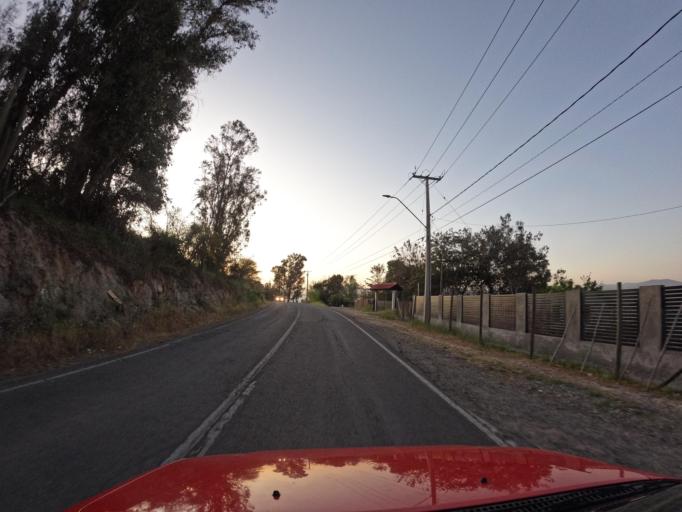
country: CL
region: O'Higgins
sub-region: Provincia de Cachapoal
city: San Vicente
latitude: -34.1559
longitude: -71.4198
